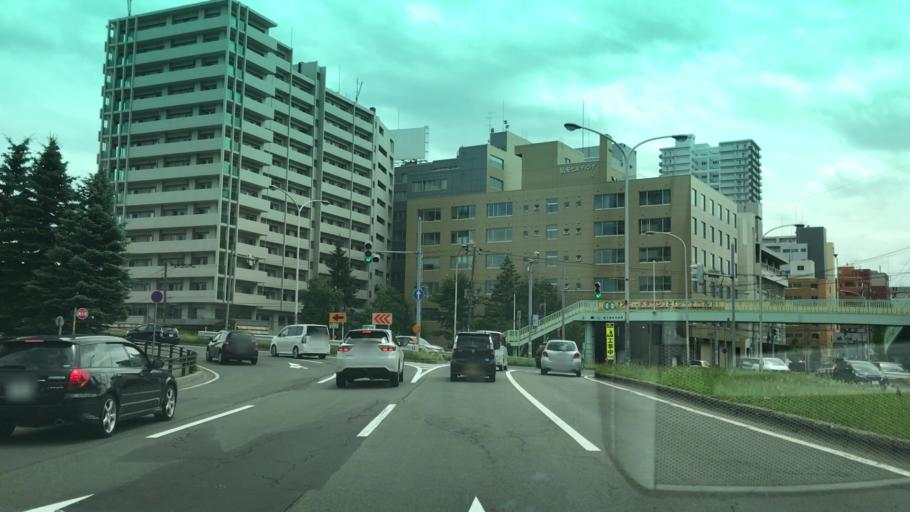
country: JP
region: Hokkaido
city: Sapporo
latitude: 43.0536
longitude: 141.3591
